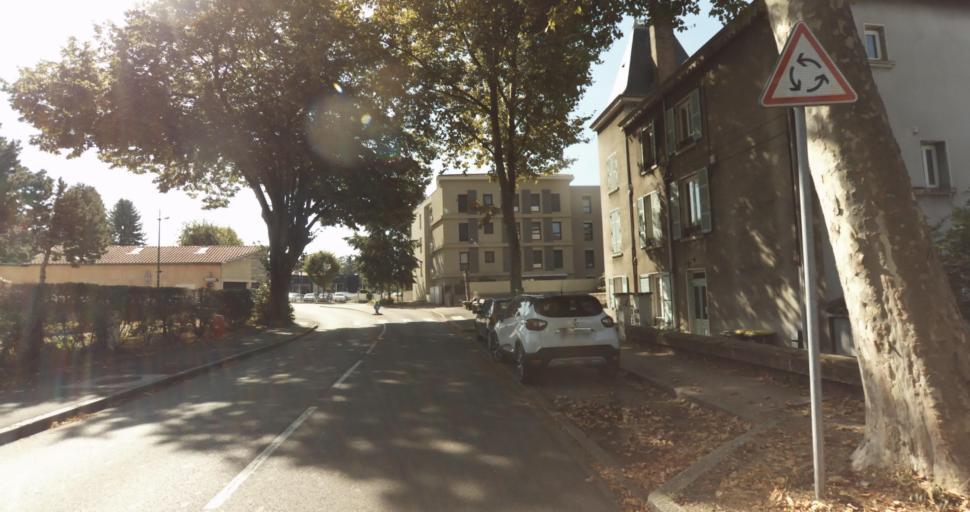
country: FR
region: Rhone-Alpes
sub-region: Departement du Rhone
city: Albigny-sur-Saone
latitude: 45.8736
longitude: 4.8399
